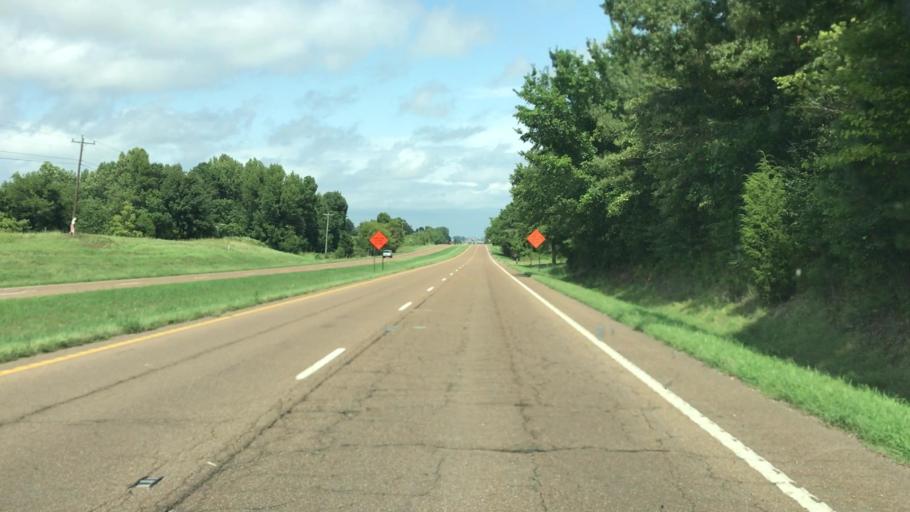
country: US
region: Tennessee
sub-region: Obion County
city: Englewood
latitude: 36.3787
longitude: -89.1140
